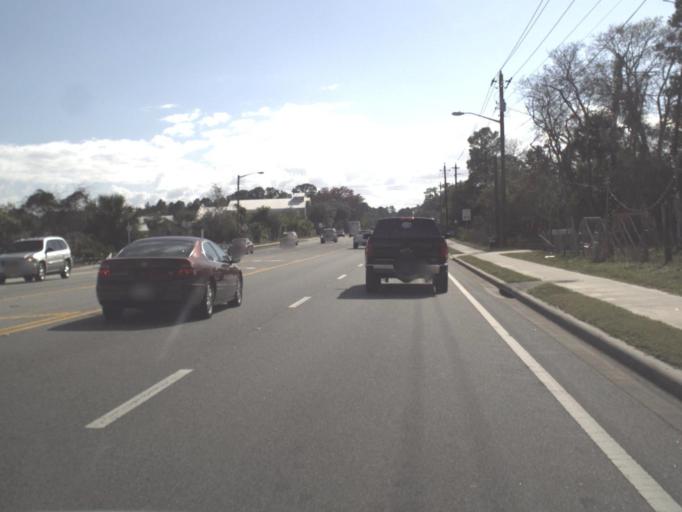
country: US
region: Florida
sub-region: Volusia County
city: South Daytona
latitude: 29.1501
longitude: -81.0352
